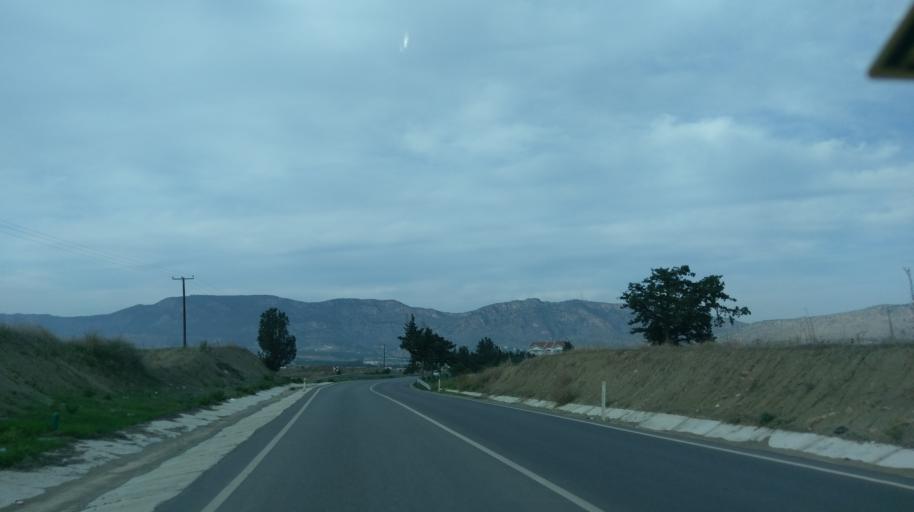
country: CY
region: Keryneia
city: Kyrenia
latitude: 35.2554
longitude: 33.2857
